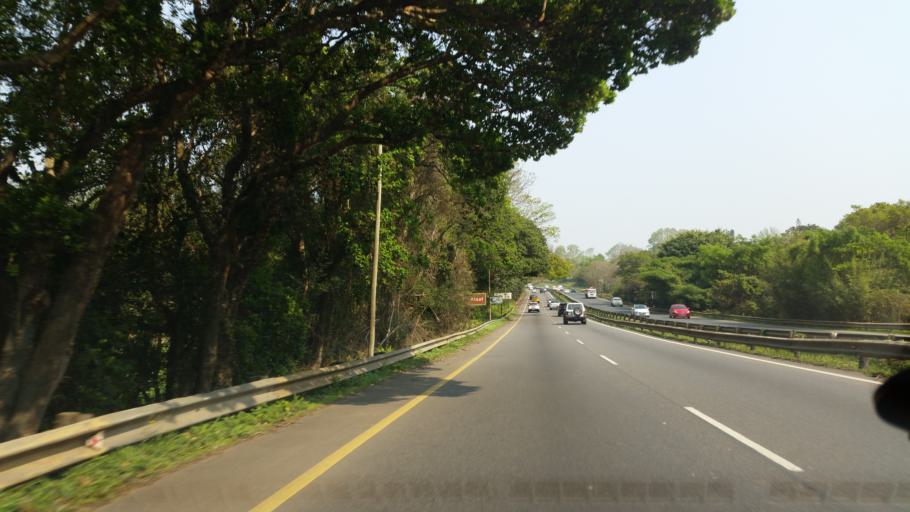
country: ZA
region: KwaZulu-Natal
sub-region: eThekwini Metropolitan Municipality
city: Berea
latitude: -29.7938
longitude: 30.8295
